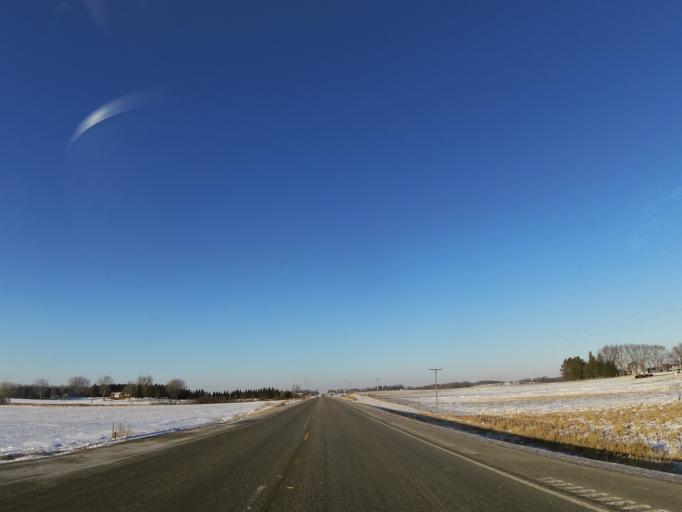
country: US
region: Minnesota
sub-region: Rice County
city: Lonsdale
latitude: 44.5018
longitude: -93.4426
